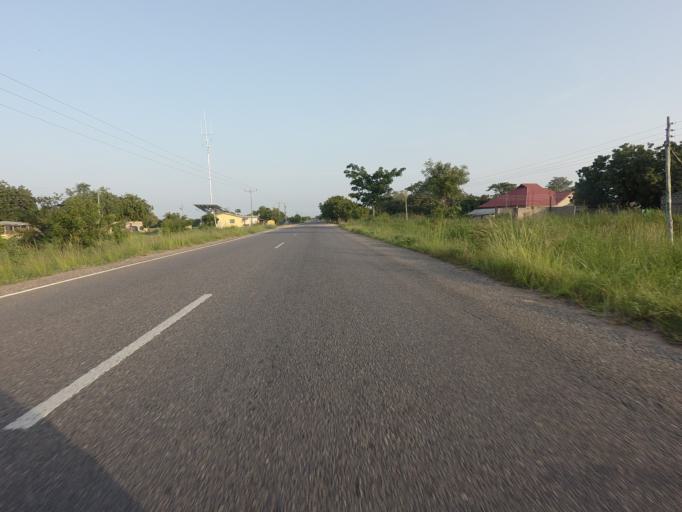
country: GH
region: Volta
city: Anloga
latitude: 5.9086
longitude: 0.7101
